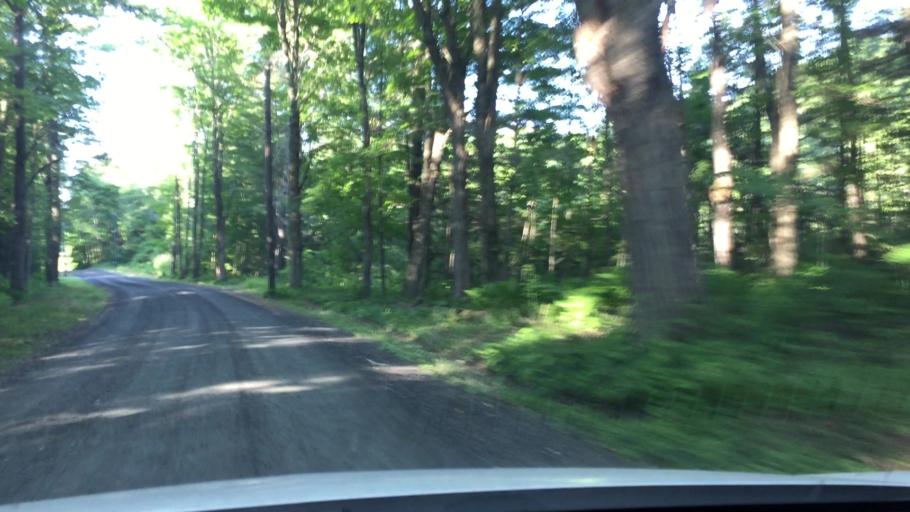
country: US
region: Massachusetts
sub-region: Berkshire County
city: Lee
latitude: 42.2668
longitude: -73.2031
